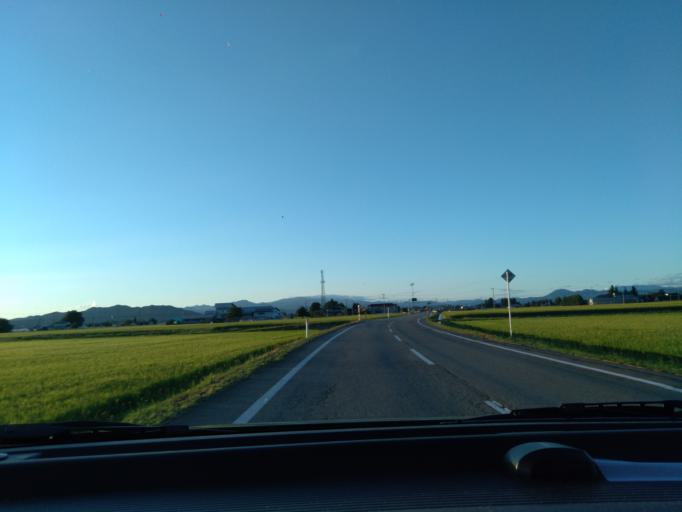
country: JP
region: Akita
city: Omagari
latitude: 39.4926
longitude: 140.5596
